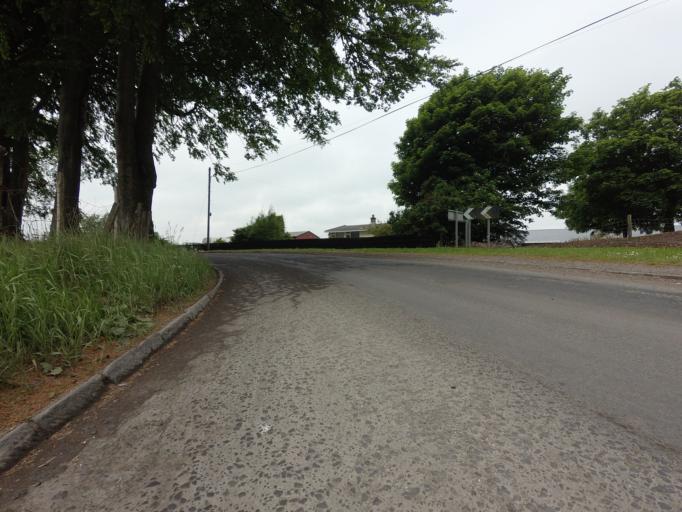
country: GB
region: Scotland
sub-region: Fife
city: Townhill
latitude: 56.0988
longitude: -3.4453
